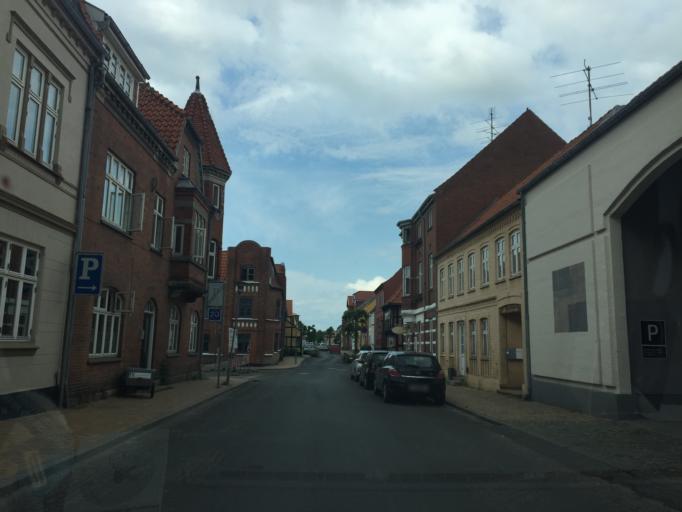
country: DK
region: South Denmark
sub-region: Assens Kommune
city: Assens
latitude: 55.2702
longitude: 9.8929
